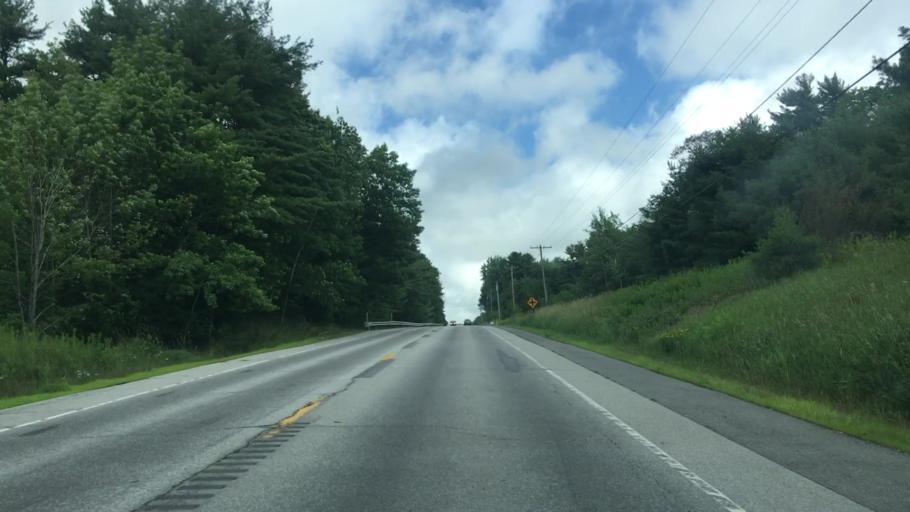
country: US
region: Maine
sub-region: Kennebec County
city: Farmingdale
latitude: 44.2574
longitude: -69.7650
